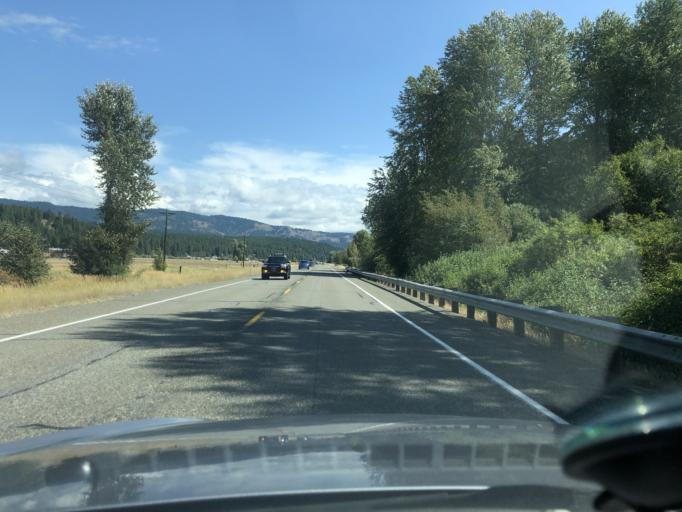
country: US
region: Washington
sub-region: Kittitas County
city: Cle Elum
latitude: 47.1863
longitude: -120.8235
